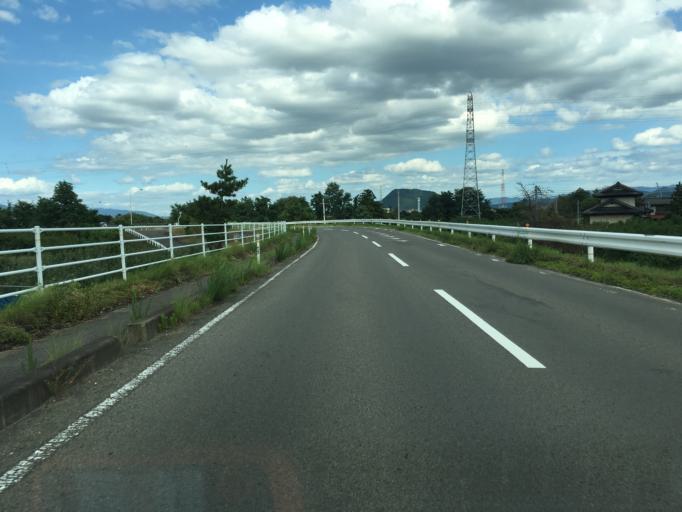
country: JP
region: Fukushima
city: Fukushima-shi
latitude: 37.7521
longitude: 140.4176
